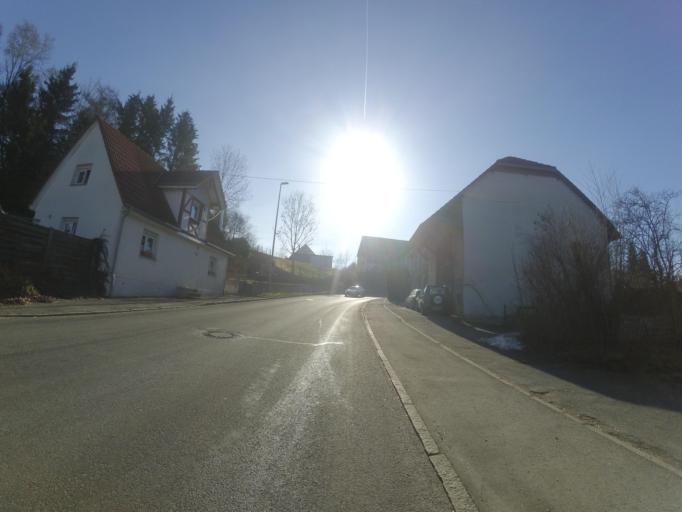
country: DE
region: Baden-Wuerttemberg
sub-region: Tuebingen Region
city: Aulendorf
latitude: 47.9319
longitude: 9.6405
